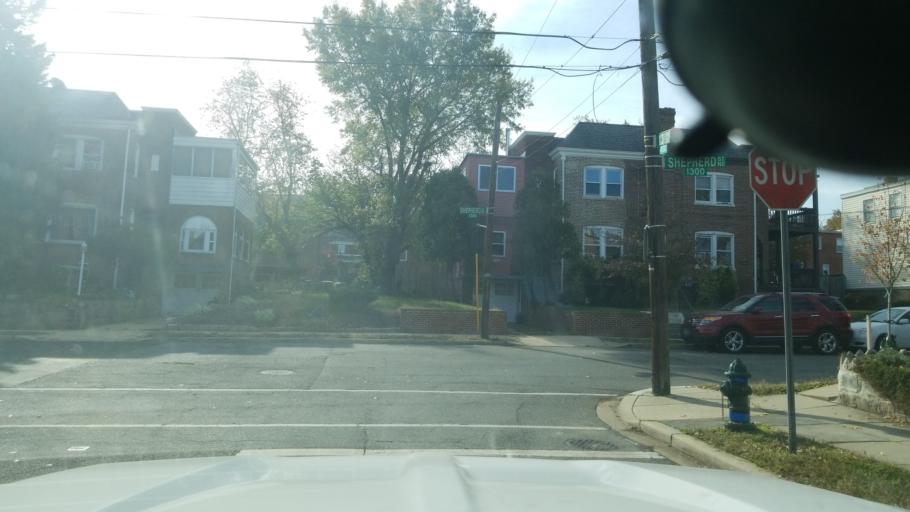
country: US
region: Maryland
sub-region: Prince George's County
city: Mount Rainier
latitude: 38.9398
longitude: -76.9872
